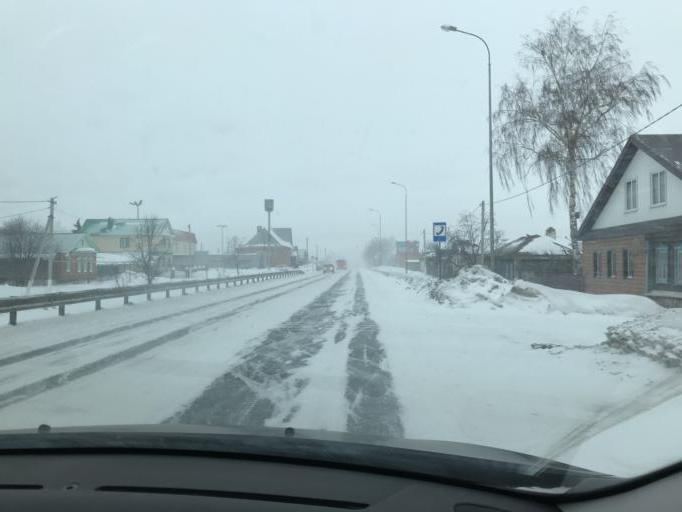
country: RU
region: Tatarstan
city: Buinsk
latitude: 54.9940
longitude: 48.3289
